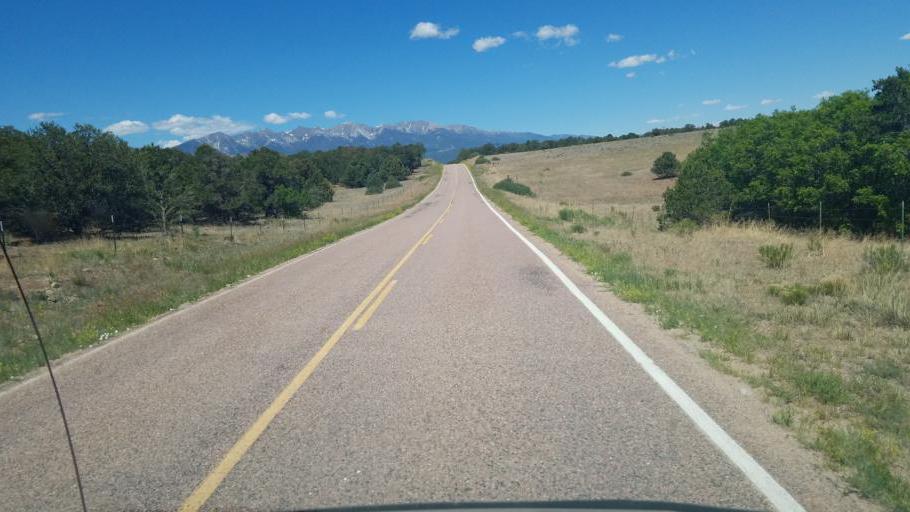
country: US
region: Colorado
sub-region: Custer County
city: Westcliffe
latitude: 38.3104
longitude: -105.6453
